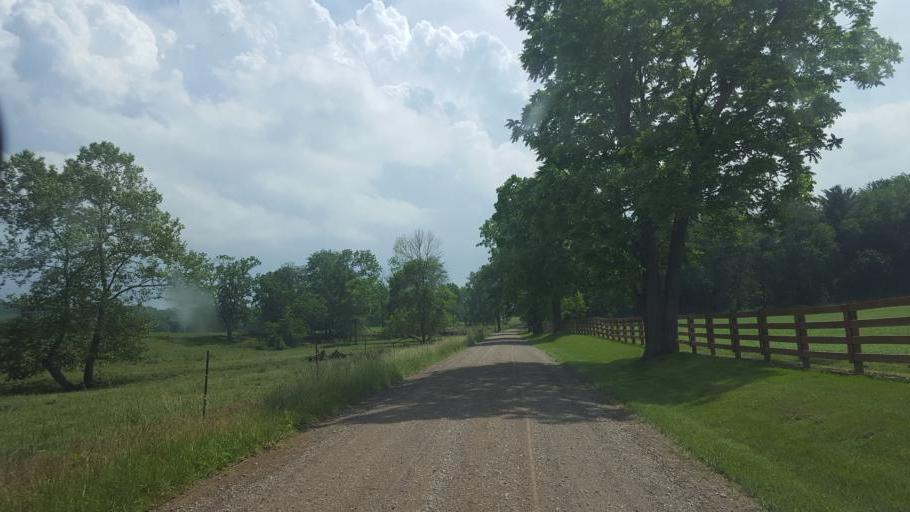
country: US
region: Ohio
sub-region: Knox County
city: Oak Hill
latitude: 40.3132
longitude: -82.2402
